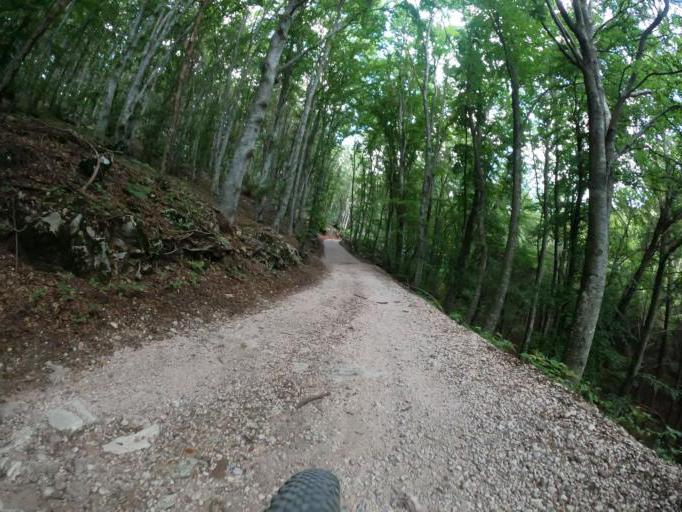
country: IT
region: Veneto
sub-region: Provincia di Verona
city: Ferrara di Monte Baldo
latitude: 45.6555
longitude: 10.8292
